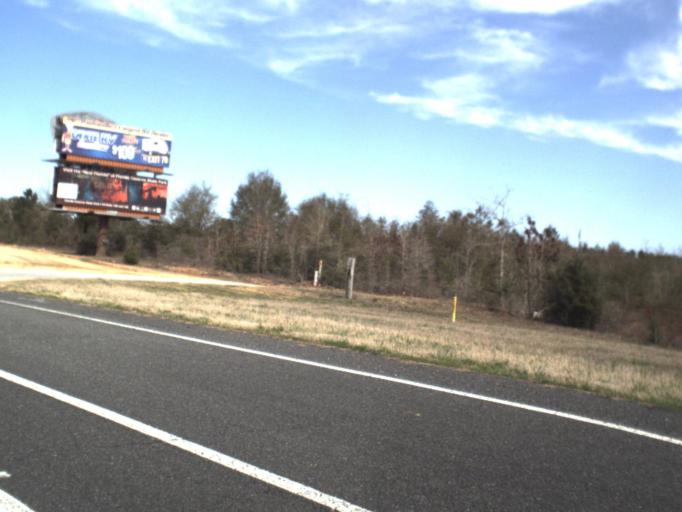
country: US
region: Florida
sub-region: Bay County
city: Youngstown
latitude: 30.5775
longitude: -85.3868
